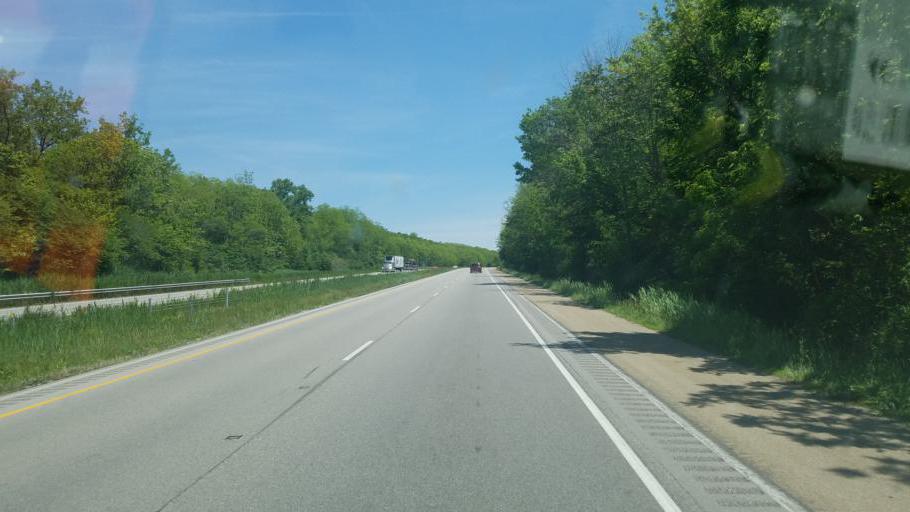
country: US
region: Illinois
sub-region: Vermilion County
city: Oakwood
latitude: 40.1274
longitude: -87.7279
